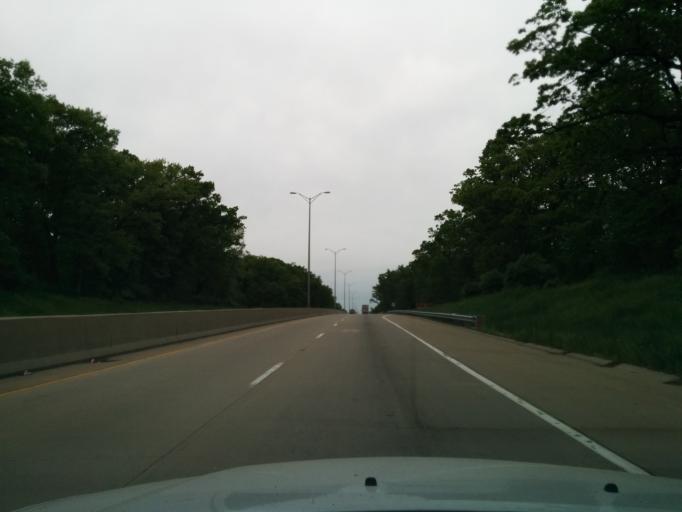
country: US
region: Illinois
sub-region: Cook County
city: Willow Springs
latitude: 41.7216
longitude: -87.8519
